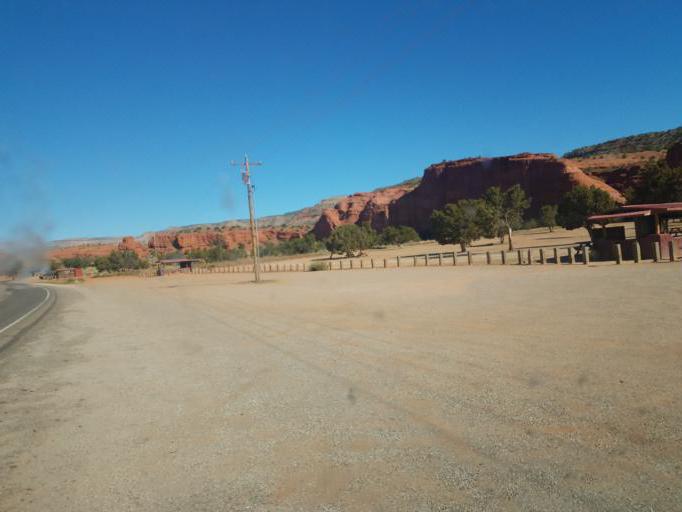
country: US
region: New Mexico
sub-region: Sandoval County
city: Jemez Pueblo
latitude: 35.6427
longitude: -106.7246
